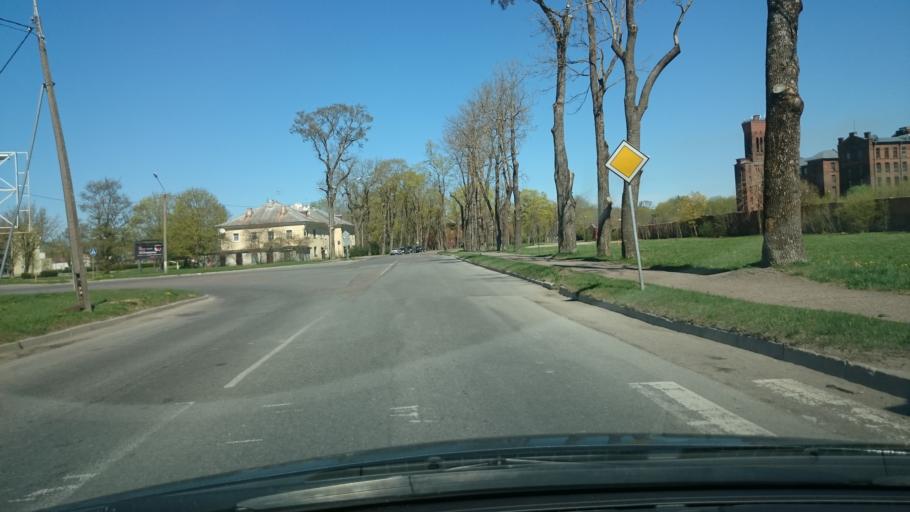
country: EE
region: Ida-Virumaa
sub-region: Narva linn
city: Narva
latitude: 59.3581
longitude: 28.1867
